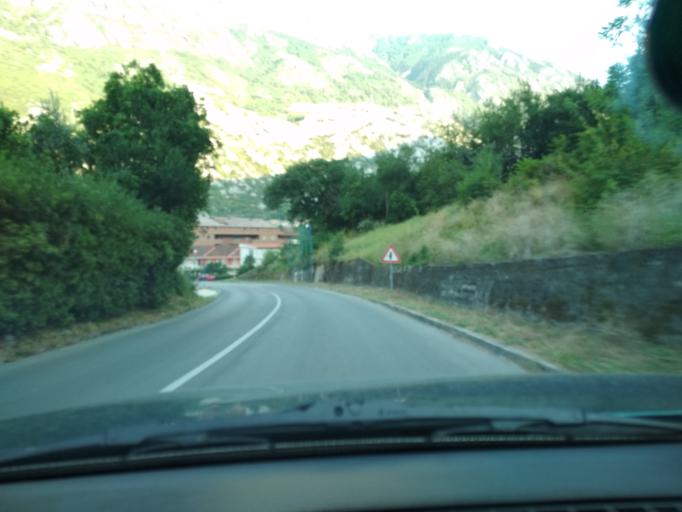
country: ME
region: Kotor
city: Kotor
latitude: 42.4167
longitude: 18.7624
